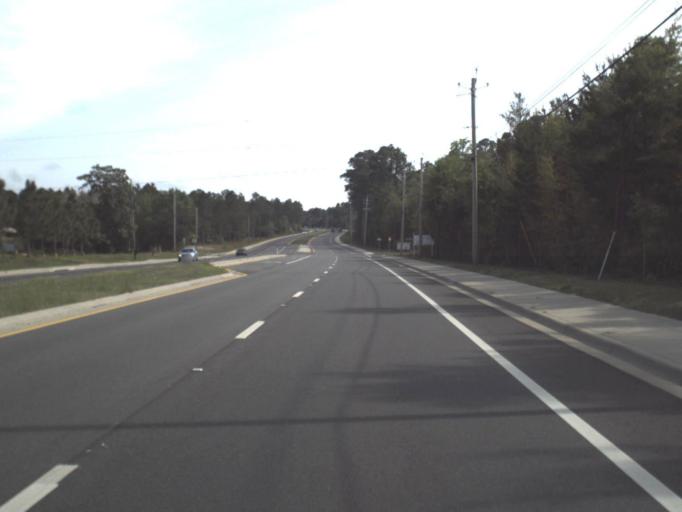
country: US
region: Florida
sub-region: Santa Rosa County
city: Holley
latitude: 30.4649
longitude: -86.9102
